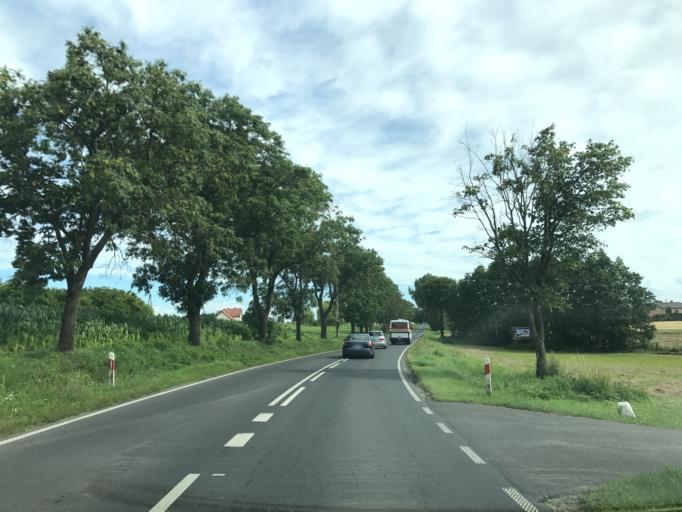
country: PL
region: Kujawsko-Pomorskie
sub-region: Powiat rypinski
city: Rypin
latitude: 53.1050
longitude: 19.3917
